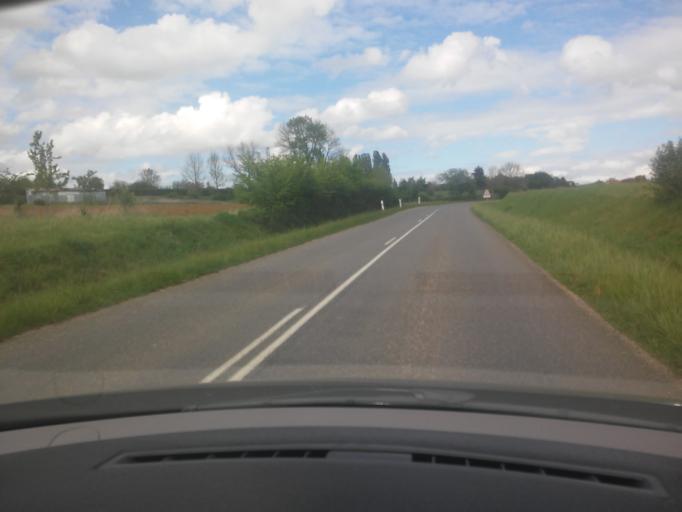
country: FR
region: Lorraine
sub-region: Departement de Meurthe-et-Moselle
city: Longuyon
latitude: 49.4105
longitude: 5.6519
